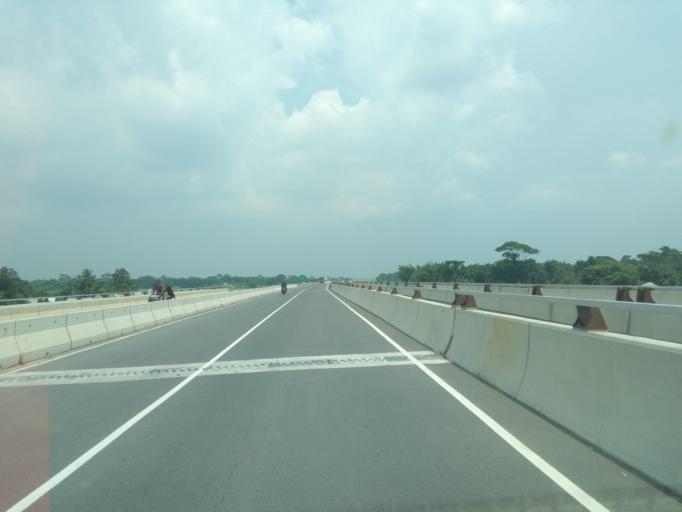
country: BD
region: Dhaka
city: Char Bhadrasan
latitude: 23.4000
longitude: 90.2085
